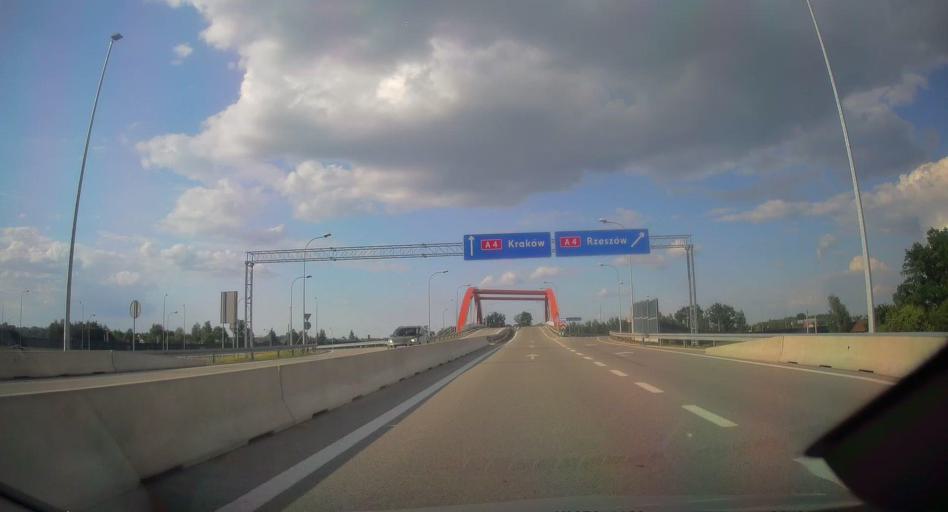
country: PL
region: Subcarpathian Voivodeship
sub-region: Powiat debicki
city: Zyrakow
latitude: 50.0776
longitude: 21.3838
